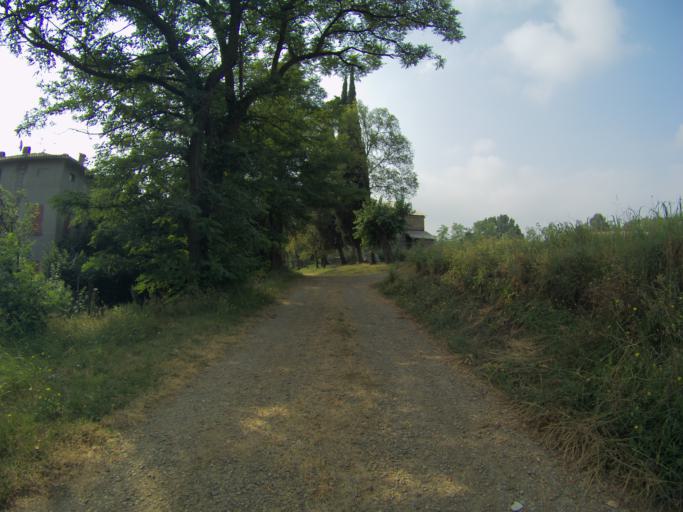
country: IT
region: Emilia-Romagna
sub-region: Provincia di Reggio Emilia
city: Pratissolo
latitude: 44.5882
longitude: 10.6590
